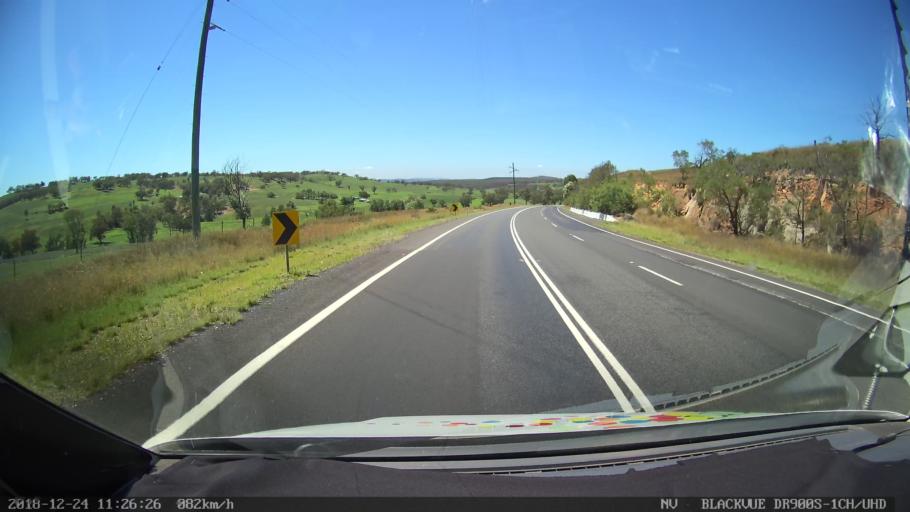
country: AU
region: New South Wales
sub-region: Upper Hunter Shire
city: Merriwa
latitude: -32.1694
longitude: 150.4312
